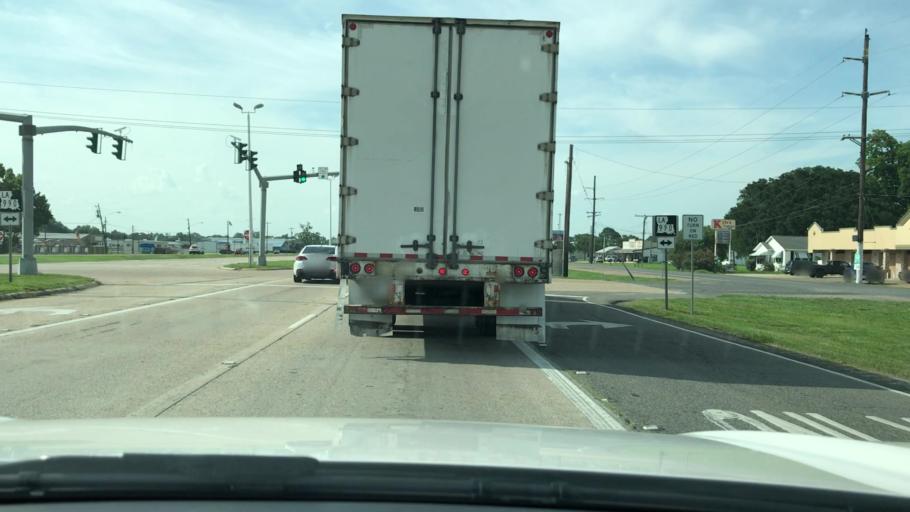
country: US
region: Louisiana
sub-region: West Baton Rouge Parish
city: Addis
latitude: 30.3554
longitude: -91.2592
